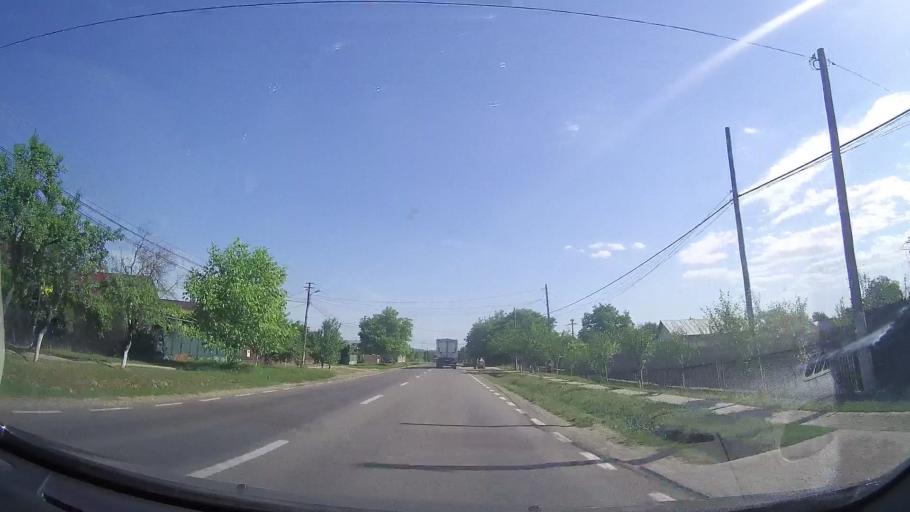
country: RO
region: Prahova
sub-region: Comuna Magurele
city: Magurele
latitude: 45.1174
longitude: 26.0338
